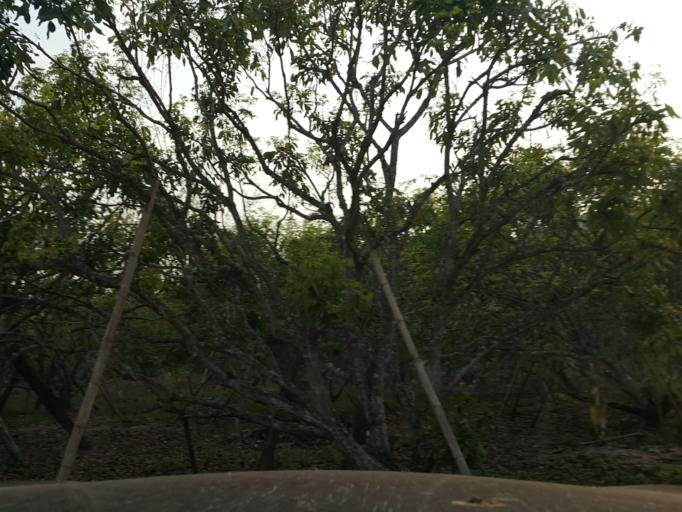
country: TH
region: Lamphun
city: Li
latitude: 17.8643
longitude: 99.0303
